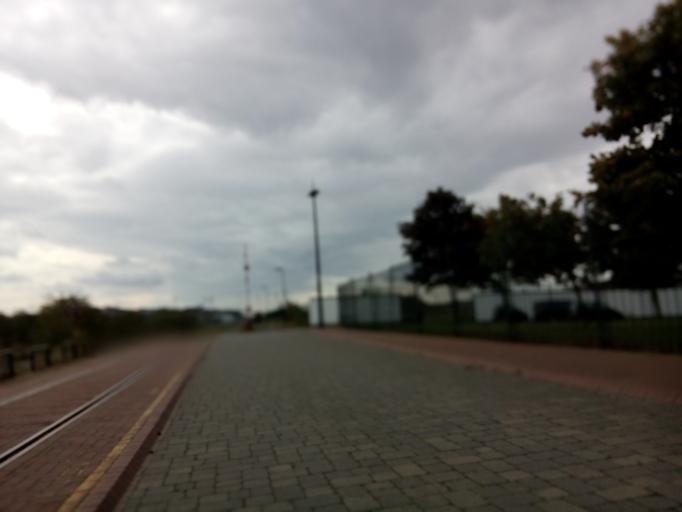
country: GB
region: England
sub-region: Suffolk
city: Ipswich
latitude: 52.0473
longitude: 1.1599
